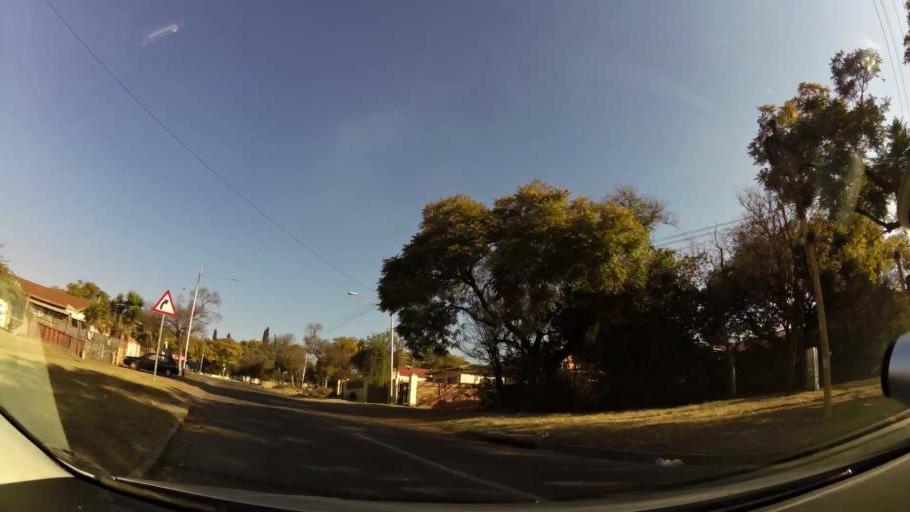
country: ZA
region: Gauteng
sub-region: City of Tshwane Metropolitan Municipality
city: Pretoria
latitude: -25.7497
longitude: 28.1419
